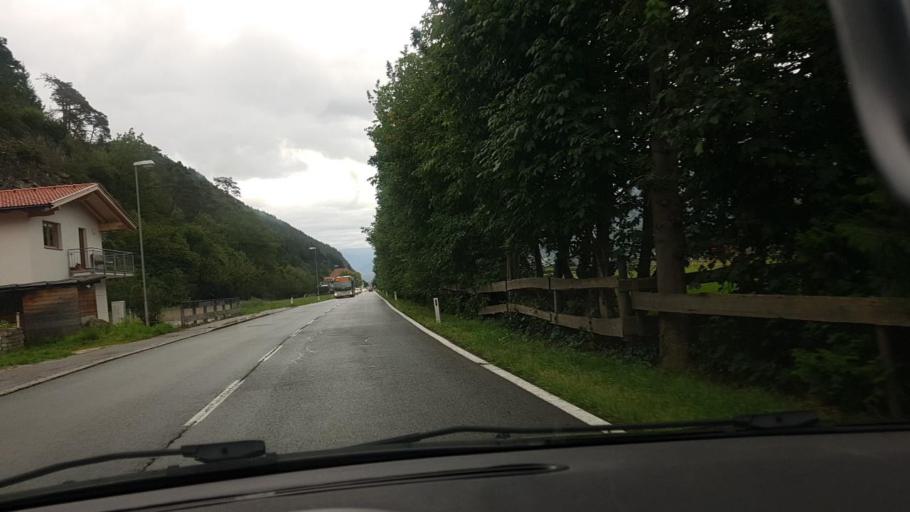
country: AT
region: Tyrol
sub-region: Politischer Bezirk Innsbruck Land
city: Pettnau
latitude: 47.3017
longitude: 11.1345
